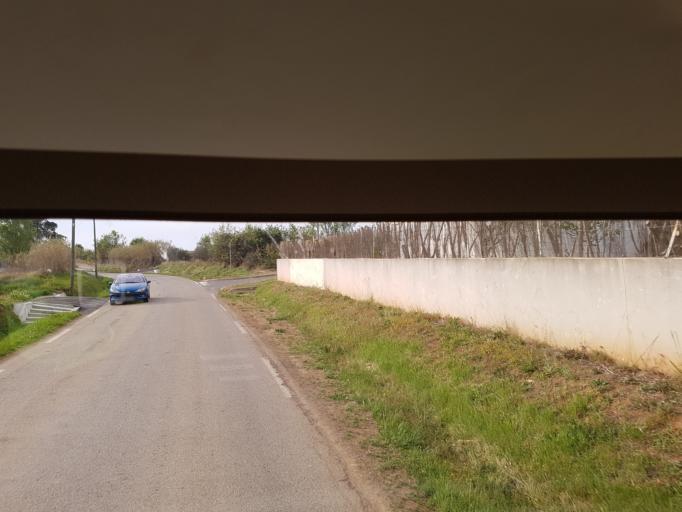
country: FR
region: Languedoc-Roussillon
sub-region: Departement de l'Herault
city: Marseillan
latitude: 43.3639
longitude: 3.5198
